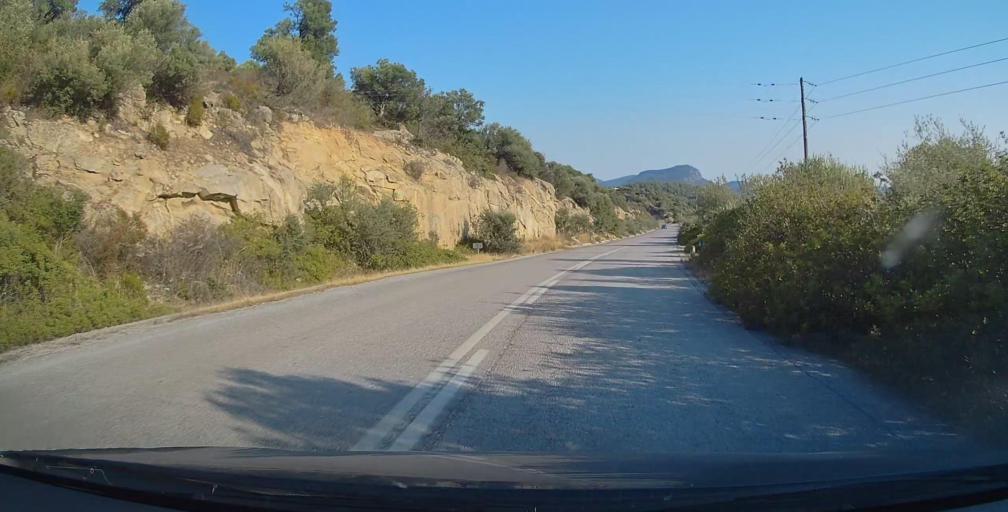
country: GR
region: Central Macedonia
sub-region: Nomos Chalkidikis
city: Sykia
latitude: 40.0084
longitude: 23.8780
